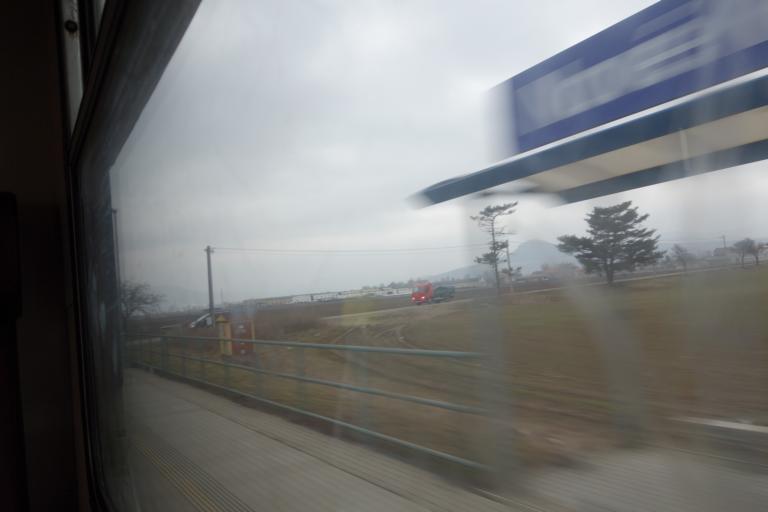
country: CZ
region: Ustecky
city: Bohusovice nad Ohri
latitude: 50.4973
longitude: 14.1206
